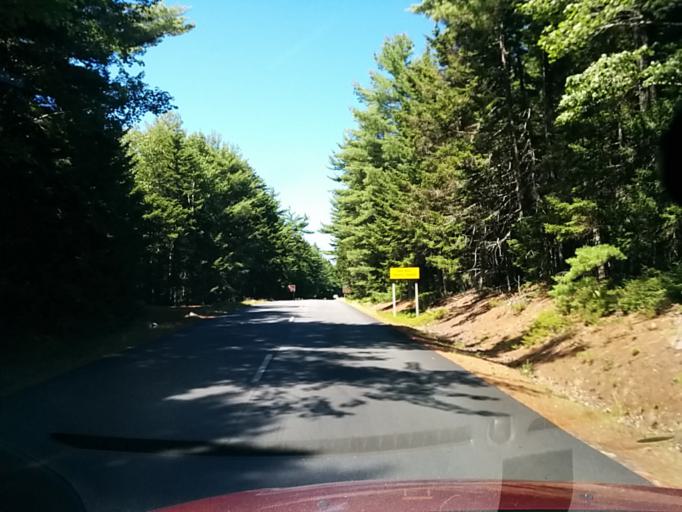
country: US
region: Maine
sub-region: Hancock County
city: Bar Harbor
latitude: 44.3121
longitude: -68.2429
